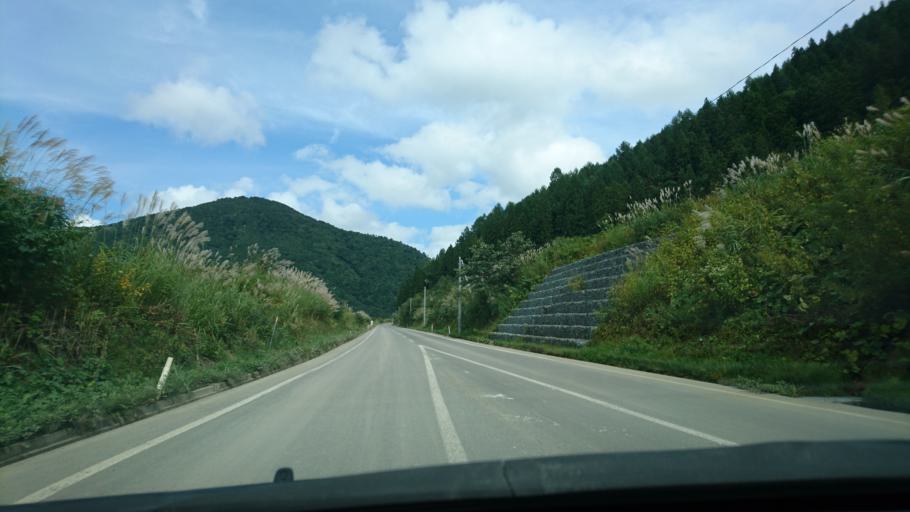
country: JP
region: Akita
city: Yuzawa
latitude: 39.0309
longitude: 140.7279
